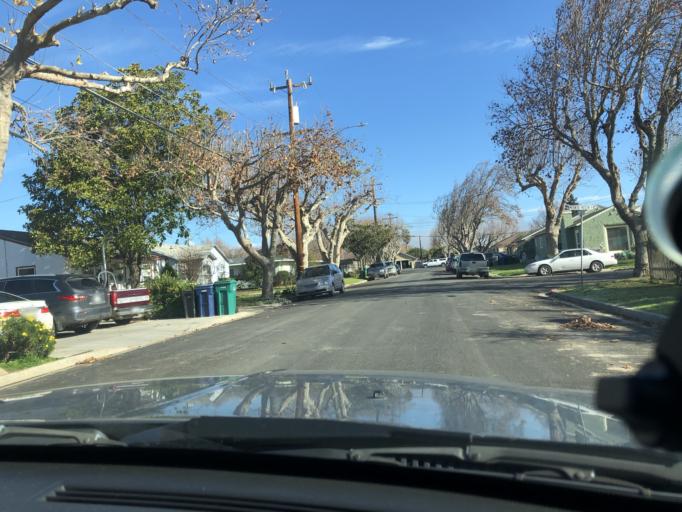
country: US
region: California
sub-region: Monterey County
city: King City
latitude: 36.2074
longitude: -121.1318
